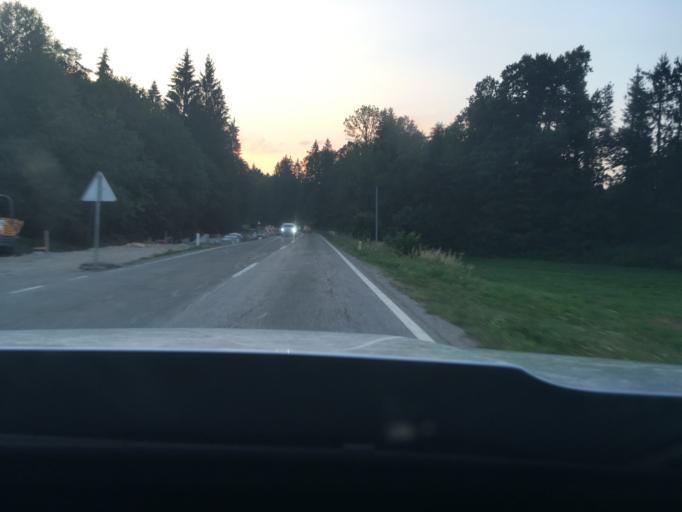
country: SI
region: Kocevje
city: Kocevje
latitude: 45.6802
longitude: 14.8230
